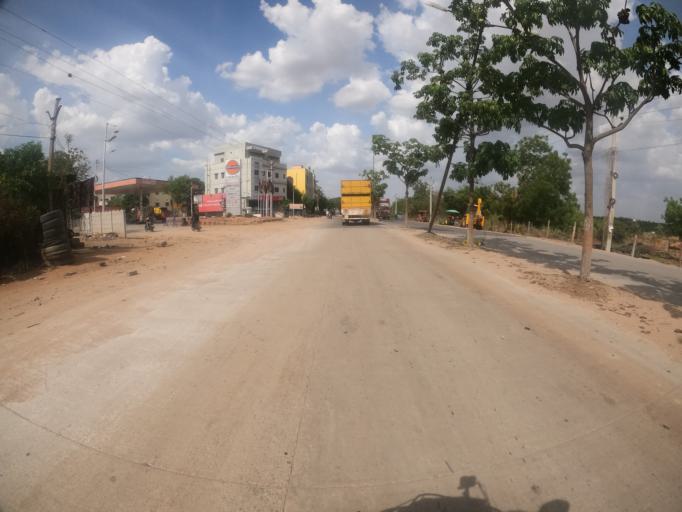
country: IN
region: Telangana
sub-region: Rangareddi
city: Sriramnagar
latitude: 17.3299
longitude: 78.2757
